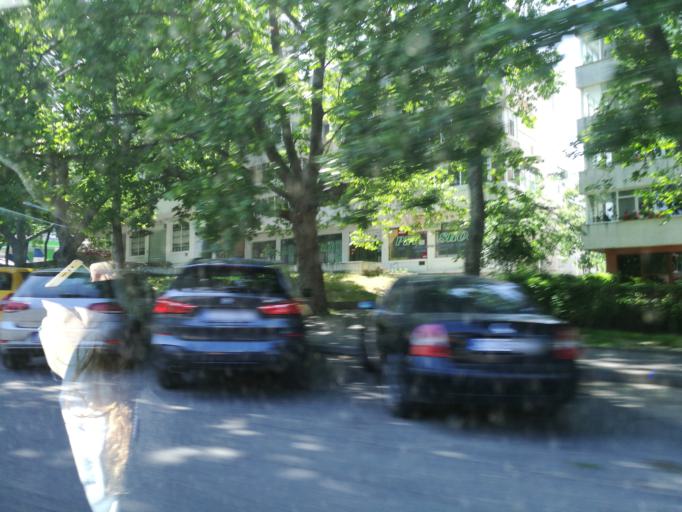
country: RO
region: Constanta
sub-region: Municipiul Constanta
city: Constanta
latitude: 44.2042
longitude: 28.6240
